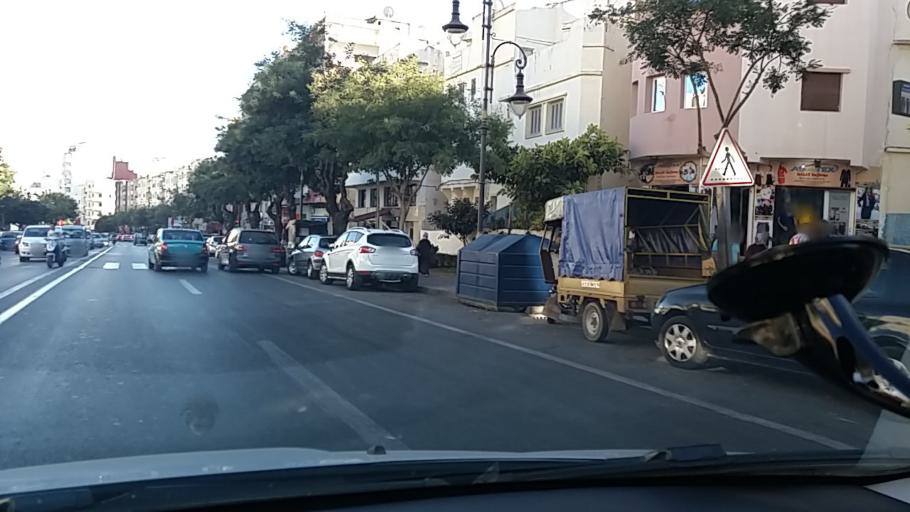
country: MA
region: Tanger-Tetouan
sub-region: Tanger-Assilah
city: Tangier
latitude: 35.7753
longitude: -5.8181
